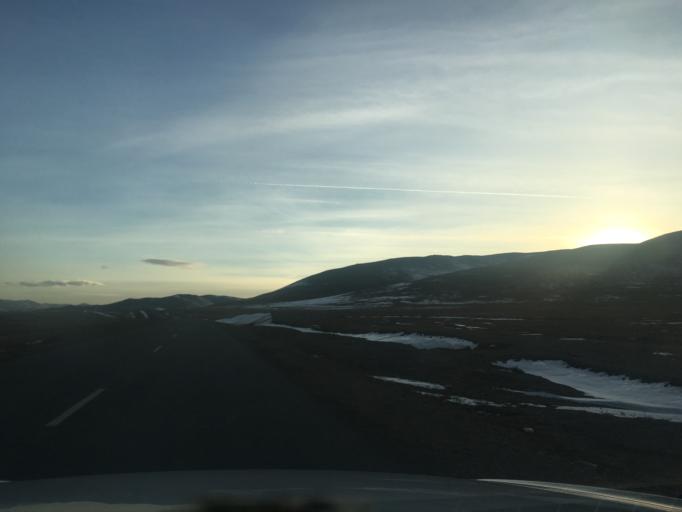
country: MN
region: Central Aimak
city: Mandal
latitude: 48.2293
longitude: 106.7180
